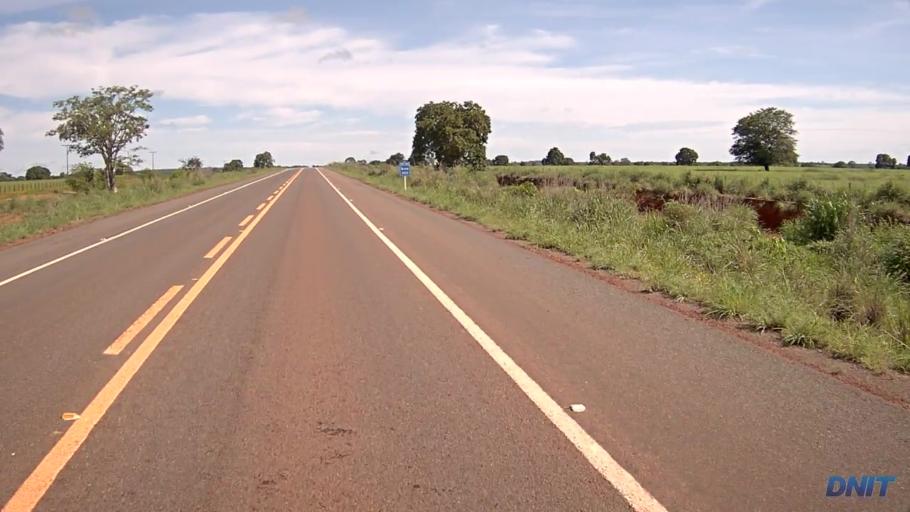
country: BR
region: Goias
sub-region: Sao Miguel Do Araguaia
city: Sao Miguel do Araguaia
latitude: -13.3730
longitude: -50.1430
